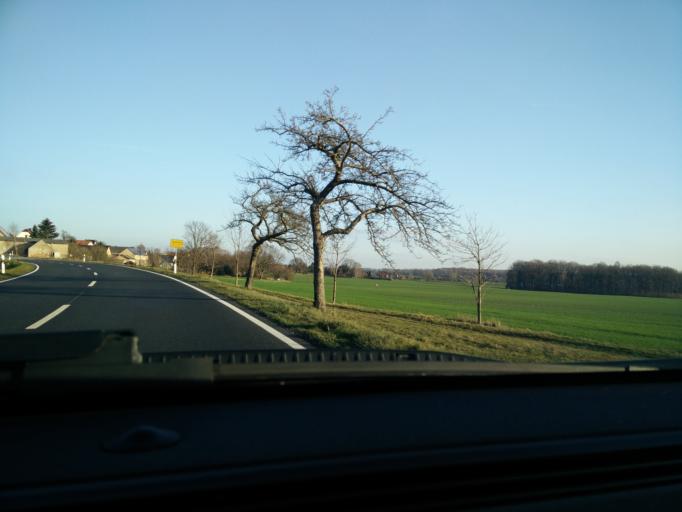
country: DE
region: Saxony
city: Bad Lausick
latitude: 51.1593
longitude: 12.6549
